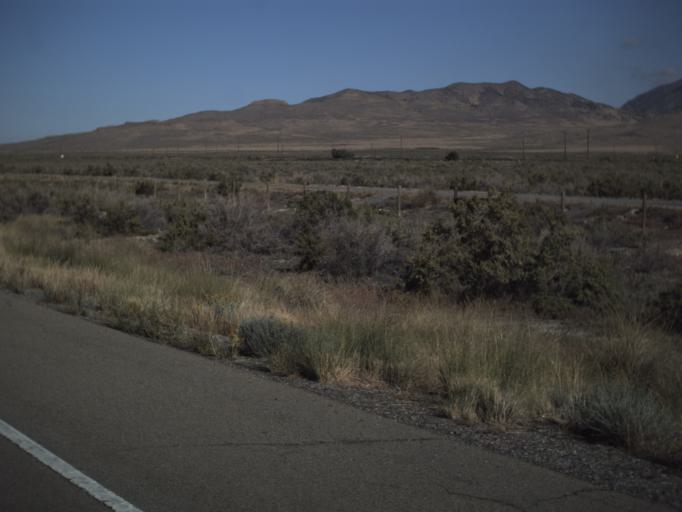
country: US
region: Utah
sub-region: Tooele County
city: Grantsville
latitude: 40.7647
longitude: -112.7843
